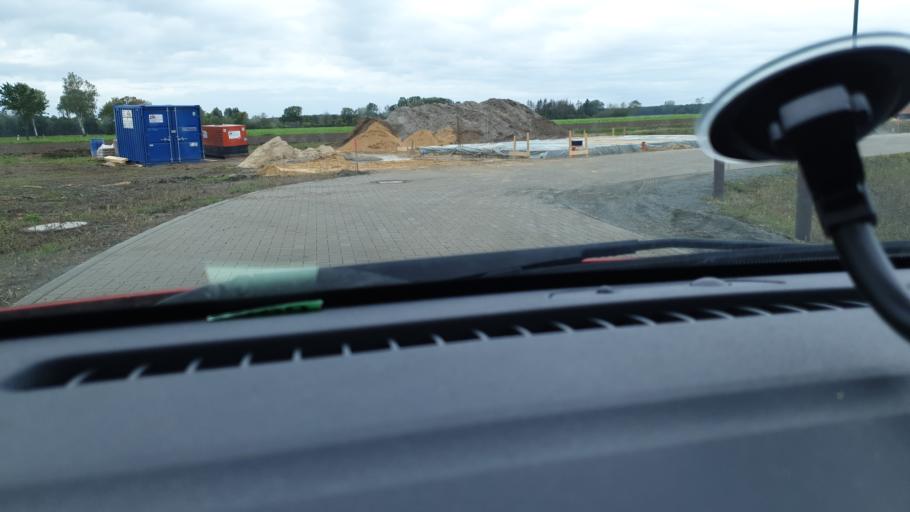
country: DE
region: Lower Saxony
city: Langlingen
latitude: 52.5530
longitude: 10.2823
